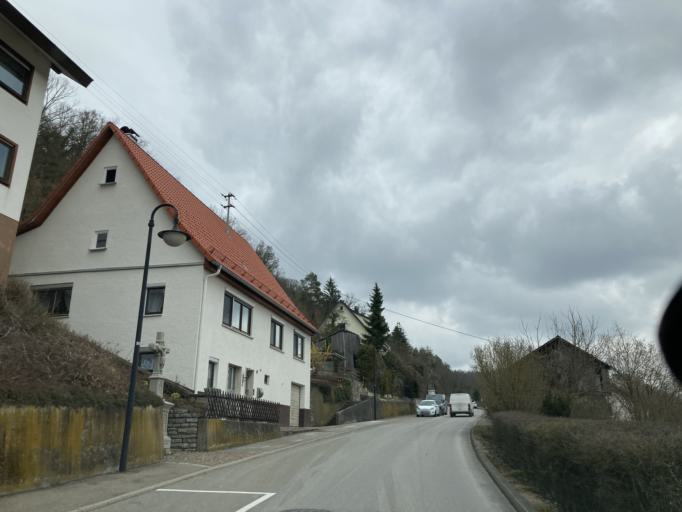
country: DE
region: Baden-Wuerttemberg
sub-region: Regierungsbezirk Stuttgart
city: Bondorf
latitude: 48.4499
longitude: 8.8047
